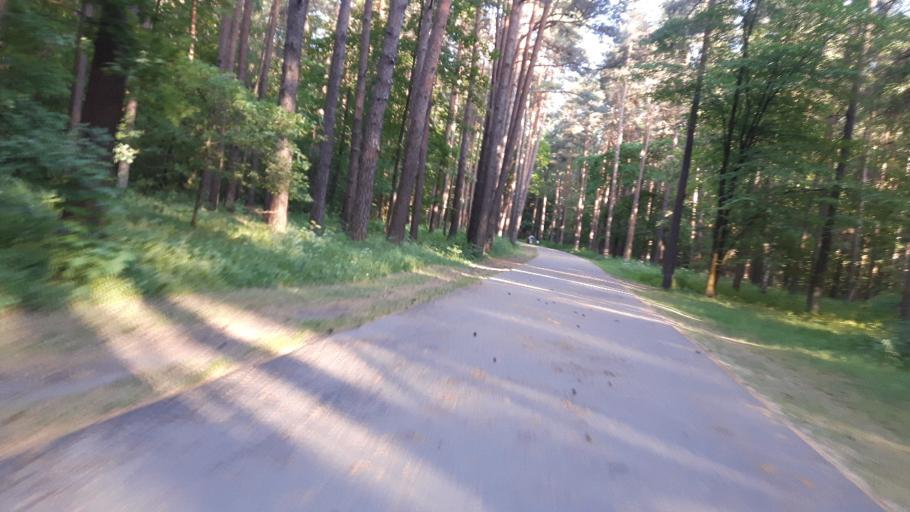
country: LV
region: Riga
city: Jaunciems
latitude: 57.0021
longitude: 24.1451
